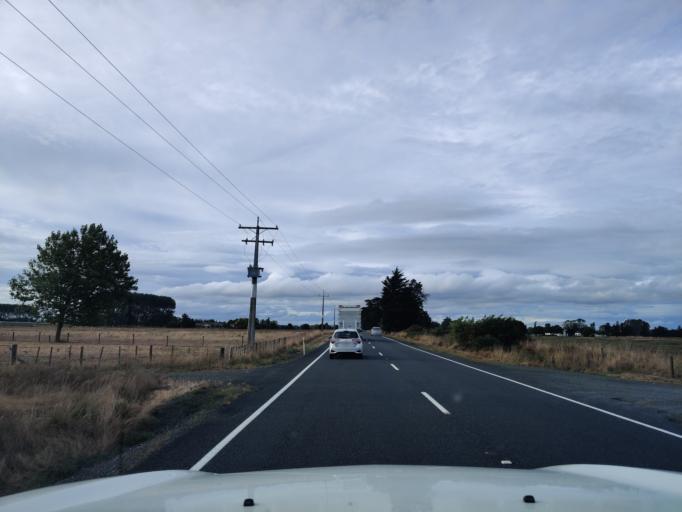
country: NZ
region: Waikato
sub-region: Hamilton City
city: Hamilton
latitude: -37.7016
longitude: 175.3381
